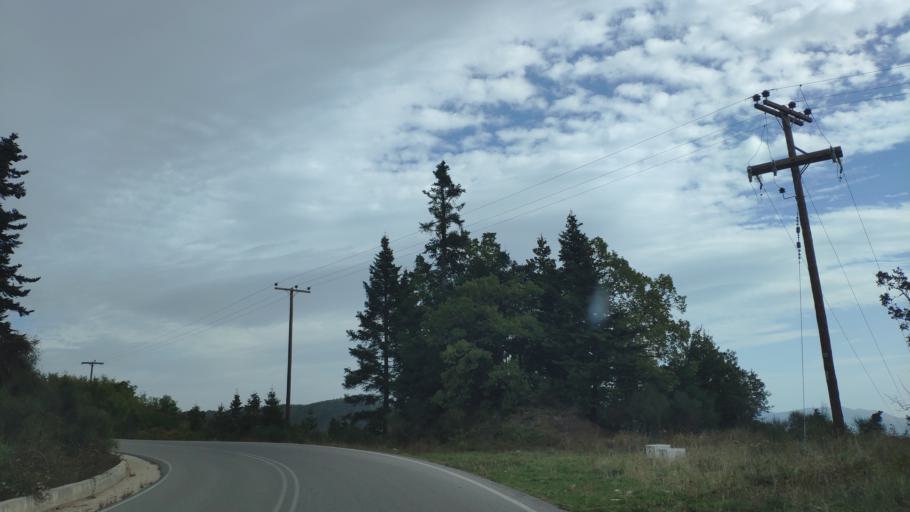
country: GR
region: Central Greece
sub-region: Nomos Fokidos
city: Amfissa
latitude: 38.6917
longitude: 22.3191
